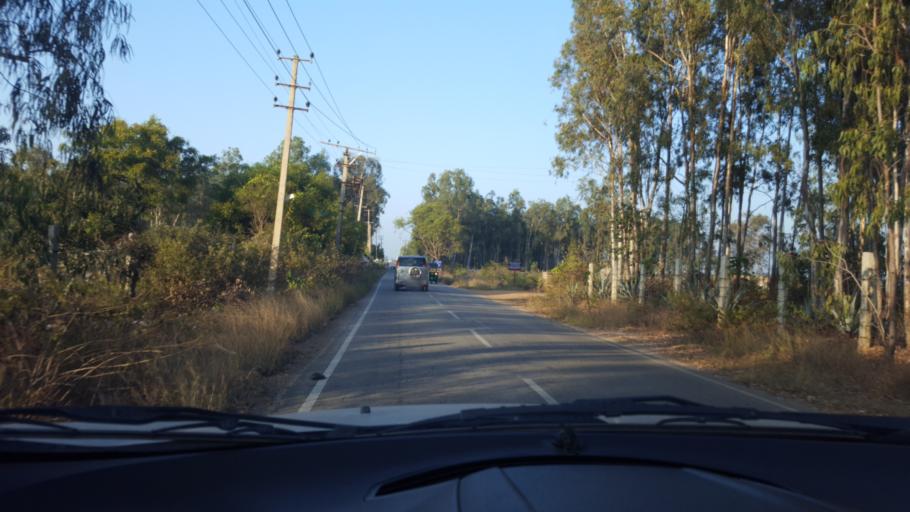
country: IN
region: Karnataka
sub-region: Bangalore Urban
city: Yelahanka
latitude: 13.1870
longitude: 77.6000
